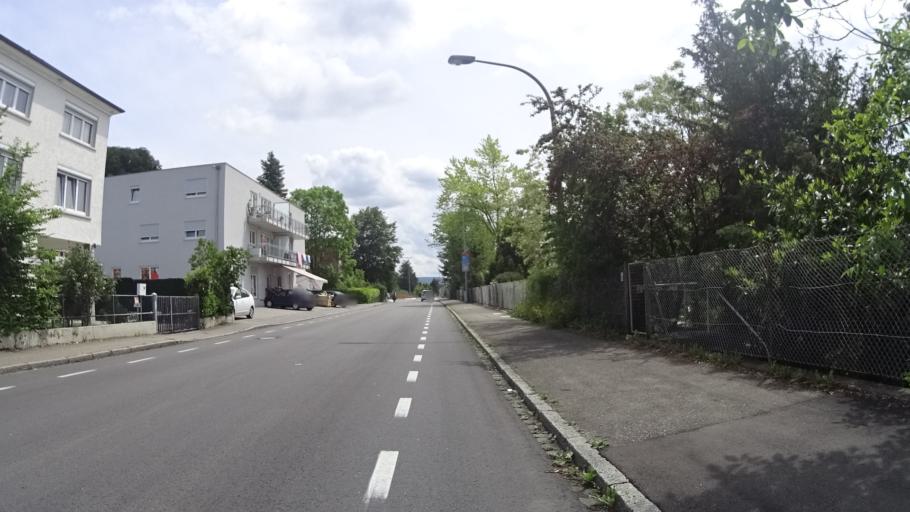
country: CH
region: Basel-Landschaft
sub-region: Bezirk Arlesheim
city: Birsfelden
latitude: 47.5596
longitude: 7.6406
